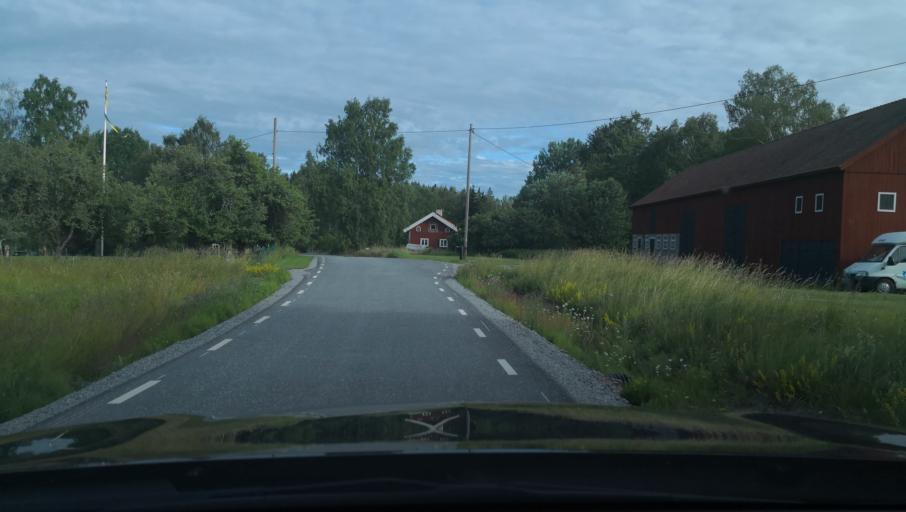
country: SE
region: Vaestmanland
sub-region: Surahammars Kommun
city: Surahammar
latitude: 59.6618
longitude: 16.1744
